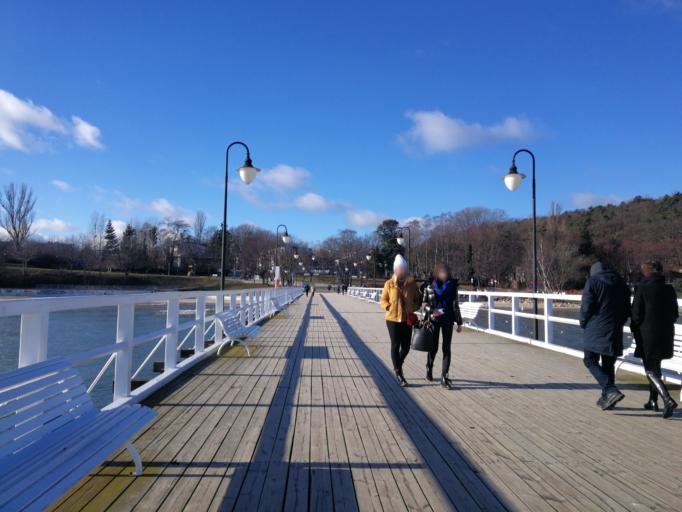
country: PL
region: Pomeranian Voivodeship
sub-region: Sopot
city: Sopot
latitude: 54.4799
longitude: 18.5659
